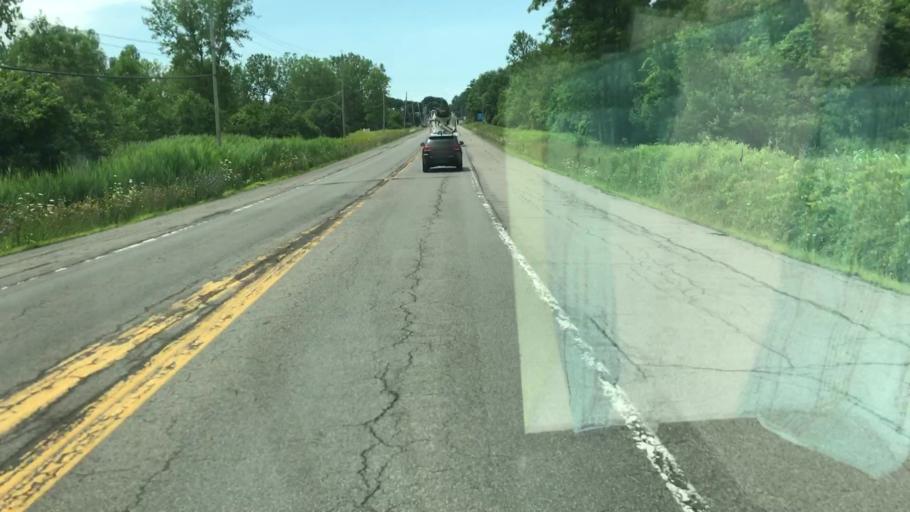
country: US
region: New York
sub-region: Onondaga County
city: Skaneateles
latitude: 42.9450
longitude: -76.4030
